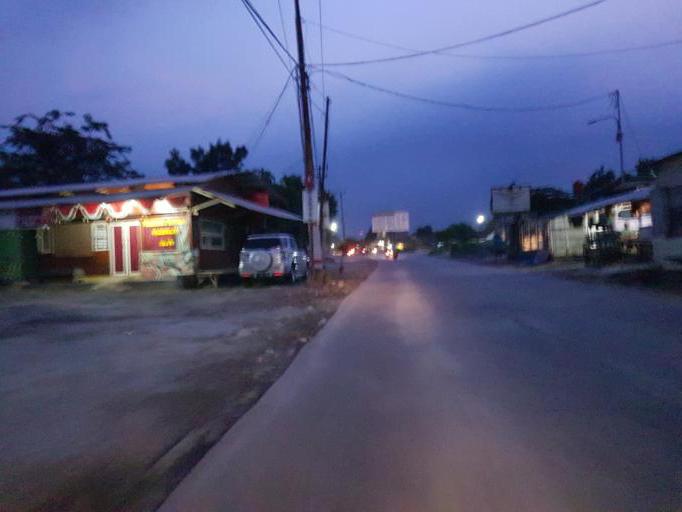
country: ID
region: West Java
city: Serpong
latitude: -6.3128
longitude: 106.6557
